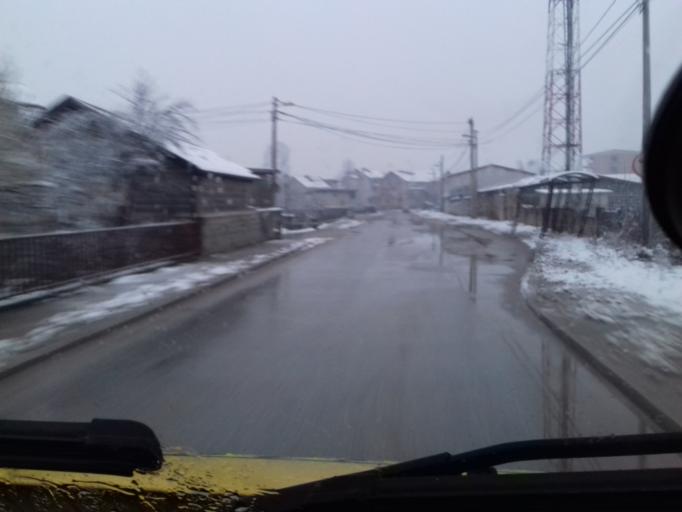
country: BA
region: Federation of Bosnia and Herzegovina
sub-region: Kanton Sarajevo
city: Sarajevo
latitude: 43.8148
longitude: 18.3282
